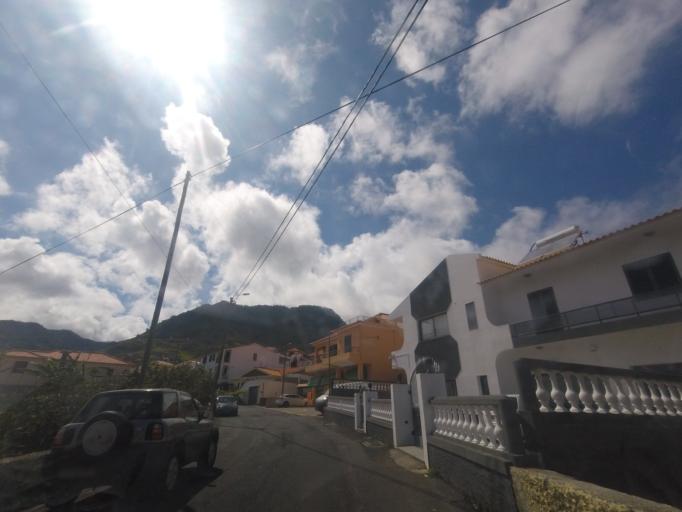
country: PT
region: Madeira
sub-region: Machico
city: Canical
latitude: 32.7403
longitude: -16.7390
